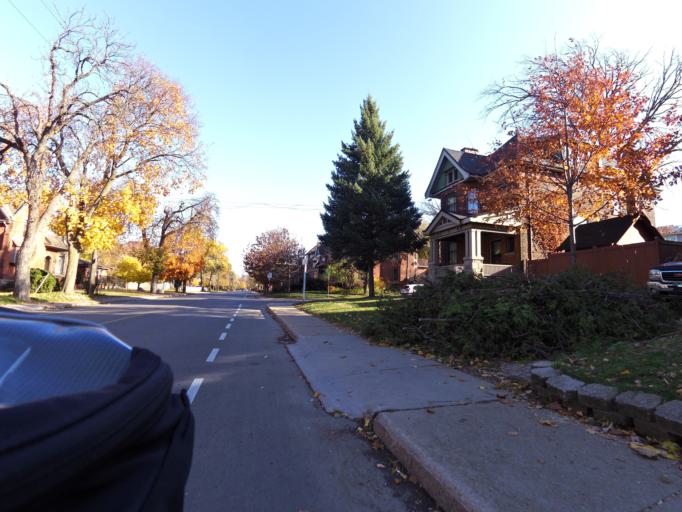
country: CA
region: Ontario
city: Hamilton
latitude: 43.2472
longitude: -79.8467
